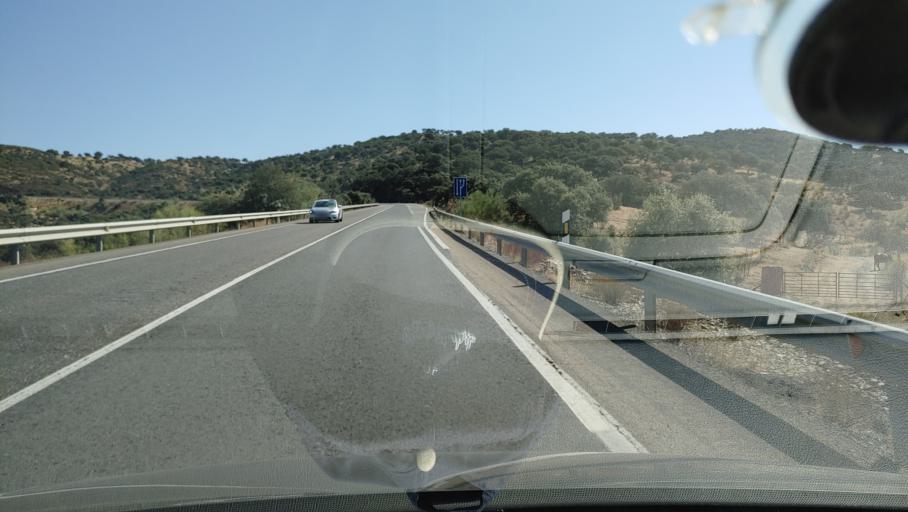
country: ES
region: Andalusia
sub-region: Province of Cordoba
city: Espiel
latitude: 38.1836
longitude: -5.0006
